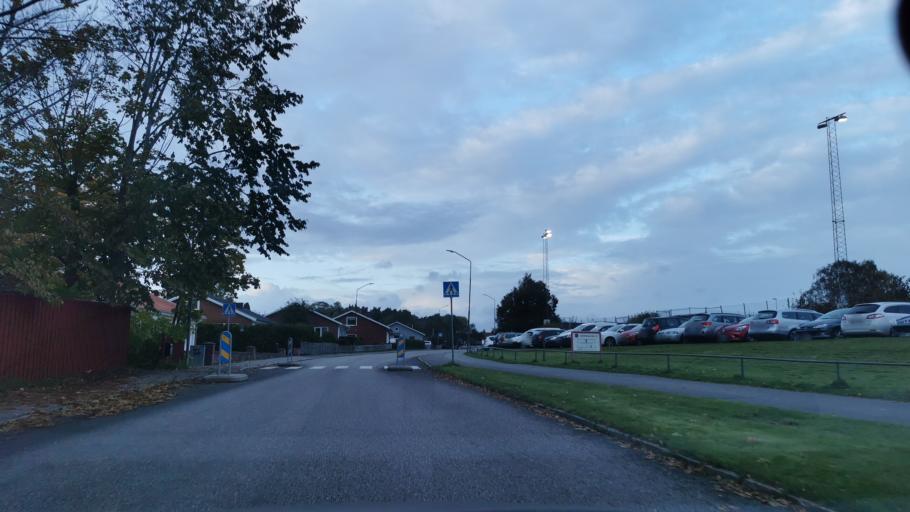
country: SE
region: Vaestra Goetaland
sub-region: Partille Kommun
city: Partille
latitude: 57.7233
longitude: 12.0778
